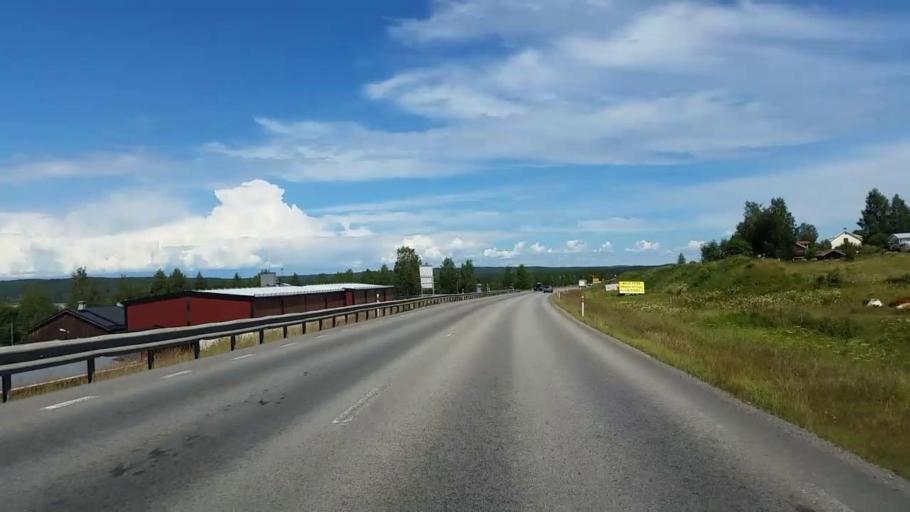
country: SE
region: Dalarna
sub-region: Rattviks Kommun
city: Raettvik
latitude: 60.8706
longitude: 15.1015
